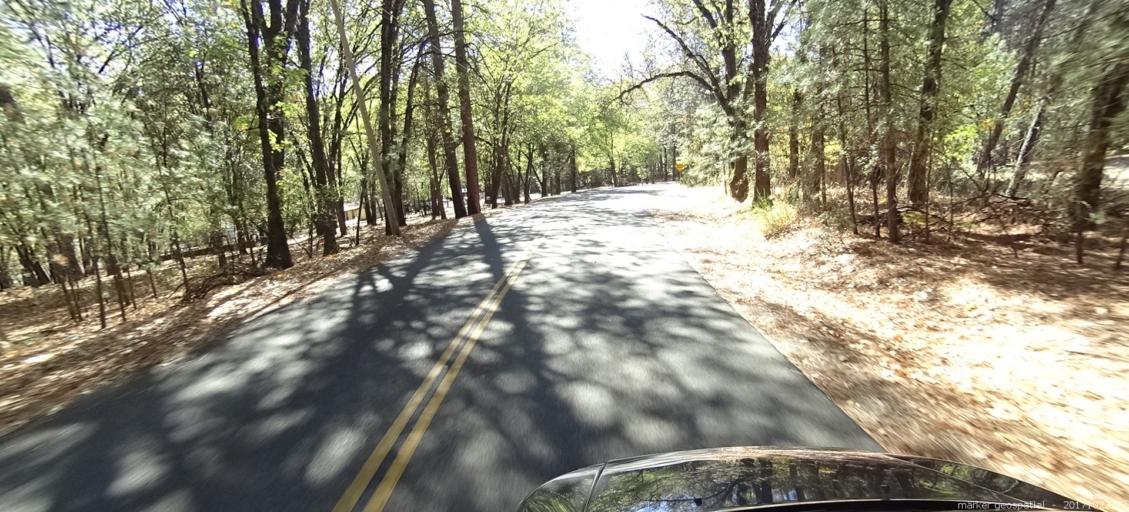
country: US
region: California
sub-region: Shasta County
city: Central Valley (historical)
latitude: 40.8710
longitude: -122.3892
